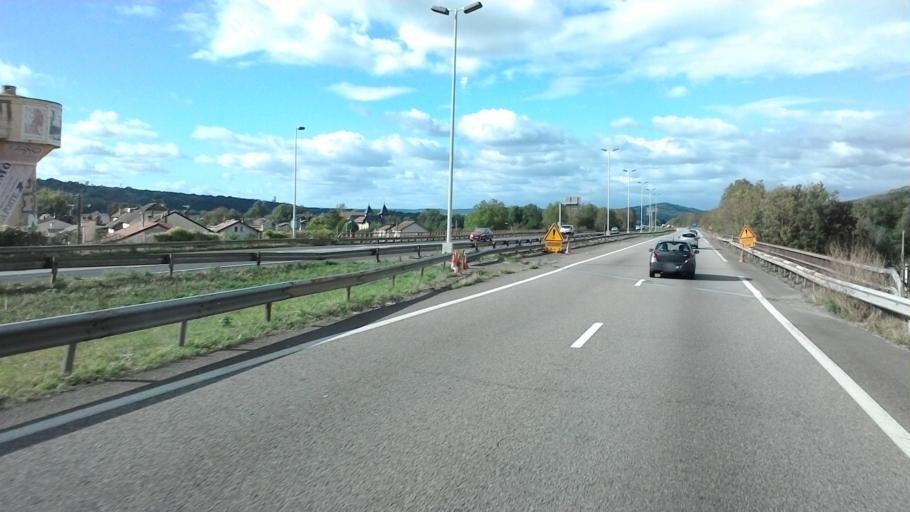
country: FR
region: Lorraine
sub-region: Departement de Meurthe-et-Moselle
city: Belleville
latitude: 48.8179
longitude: 6.1087
